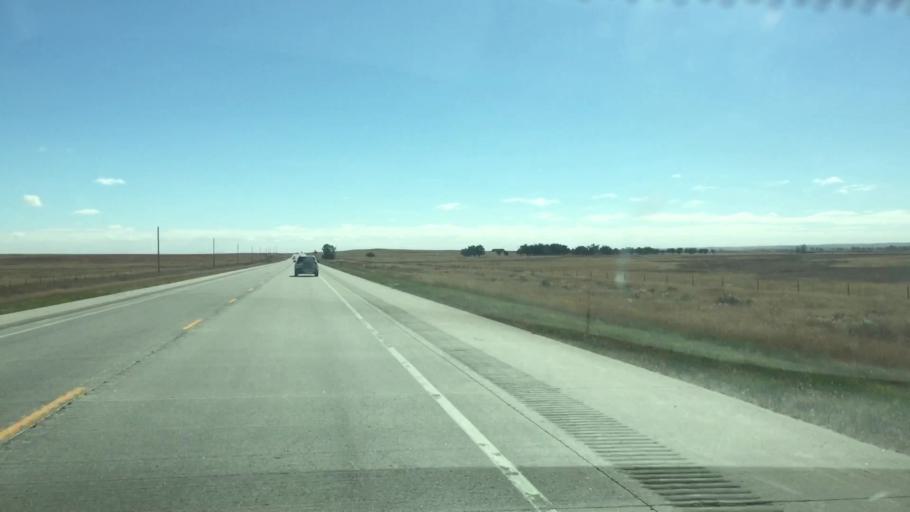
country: US
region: Colorado
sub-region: Lincoln County
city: Limon
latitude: 39.2029
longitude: -103.5832
